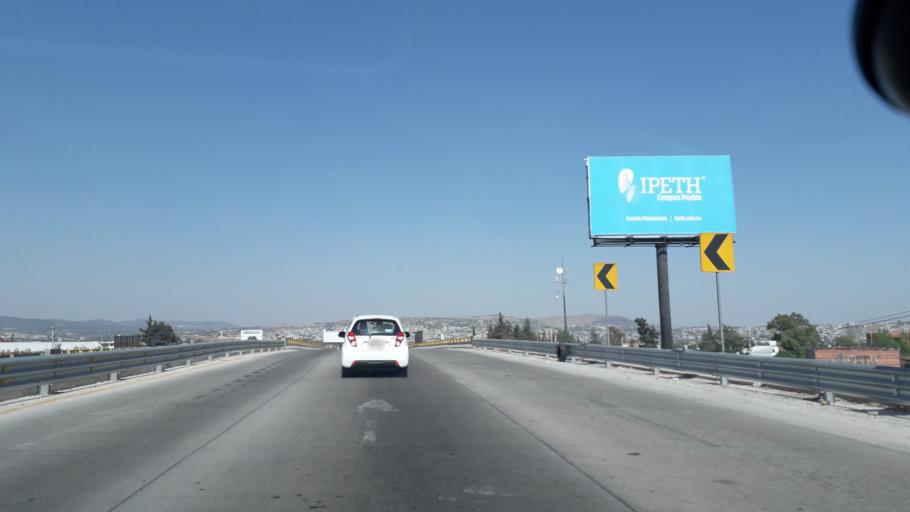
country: MX
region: Puebla
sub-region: Puebla
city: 18 de Marzo
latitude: 18.9710
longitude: -98.1992
